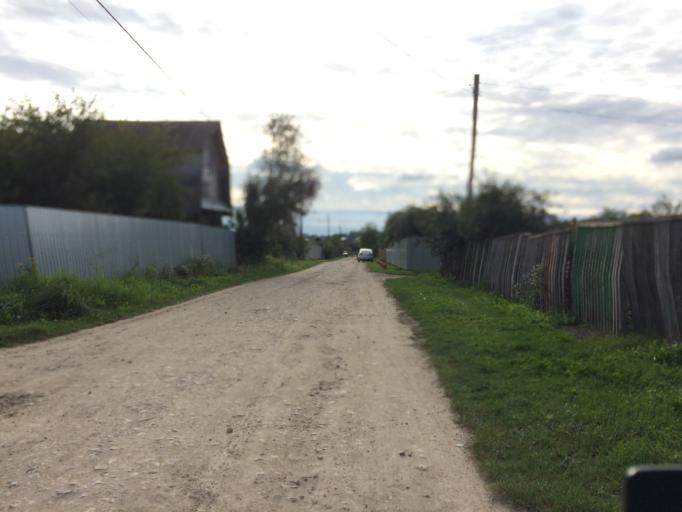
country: RU
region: Mariy-El
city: Yoshkar-Ola
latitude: 56.6550
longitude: 48.0013
